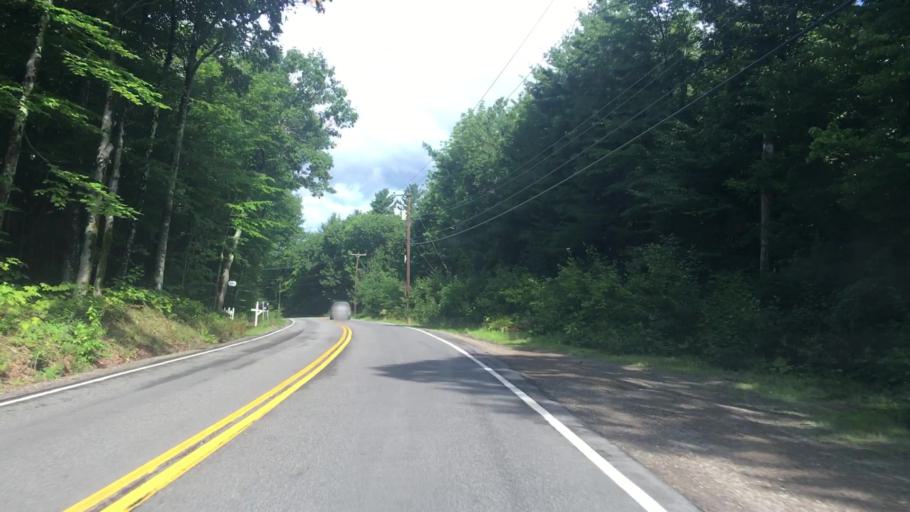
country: US
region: New Hampshire
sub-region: Belknap County
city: Gilford
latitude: 43.5626
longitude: -71.3733
